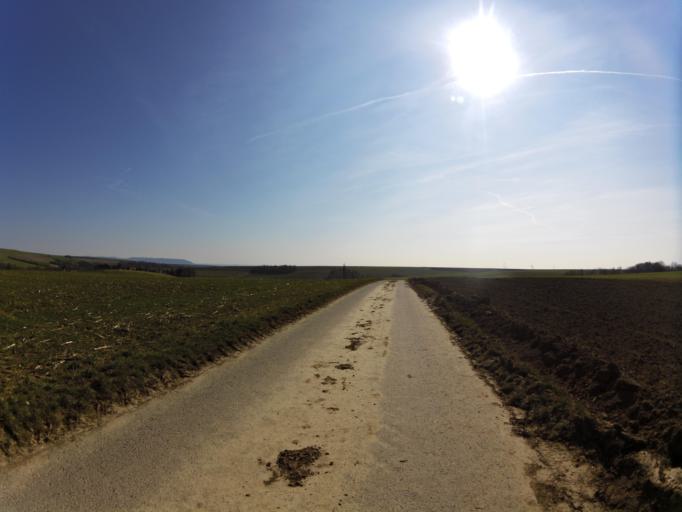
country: DE
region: Bavaria
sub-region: Regierungsbezirk Unterfranken
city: Dettelbach
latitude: 49.8238
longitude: 10.1423
